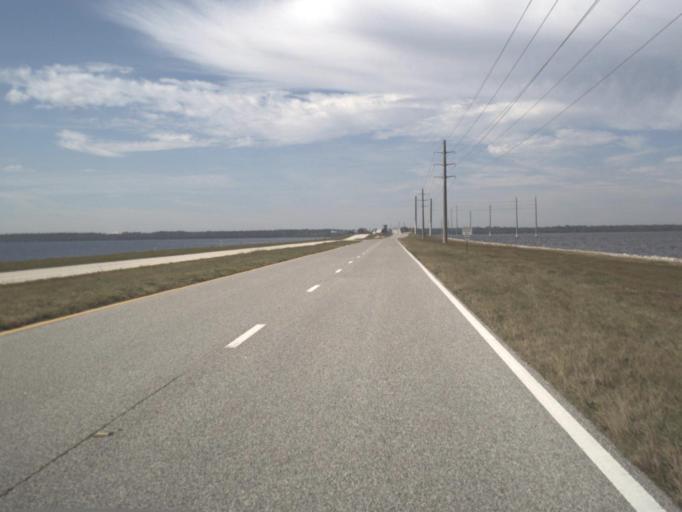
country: US
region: Florida
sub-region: Brevard County
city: Port Saint John
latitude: 28.5272
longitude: -80.7532
